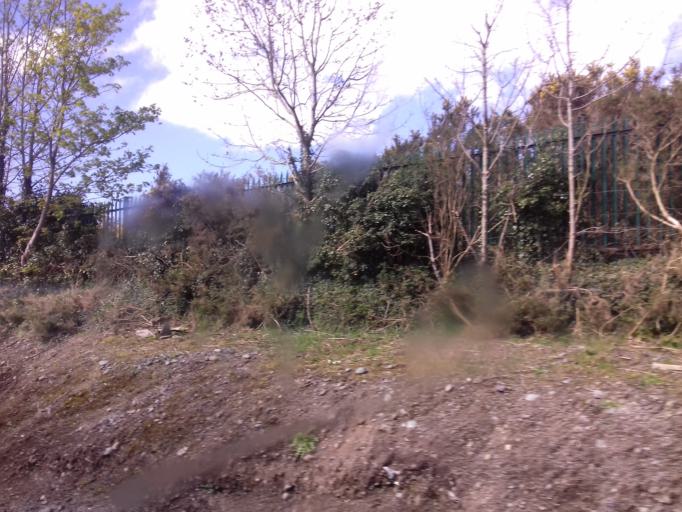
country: IE
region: Munster
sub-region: Ciarrai
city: Cill Airne
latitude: 52.0587
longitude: -9.4942
